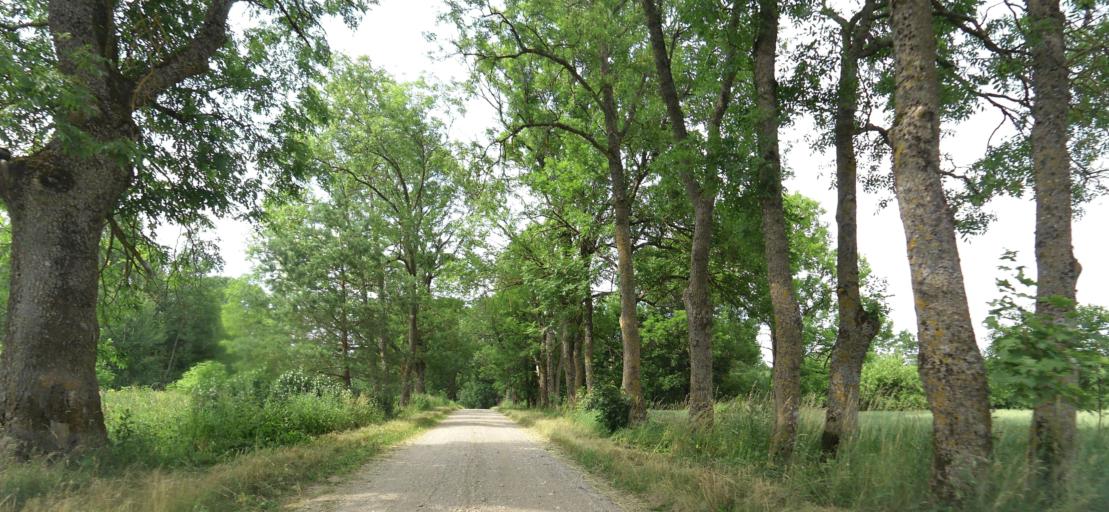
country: LT
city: Obeliai
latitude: 56.1810
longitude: 25.0444
